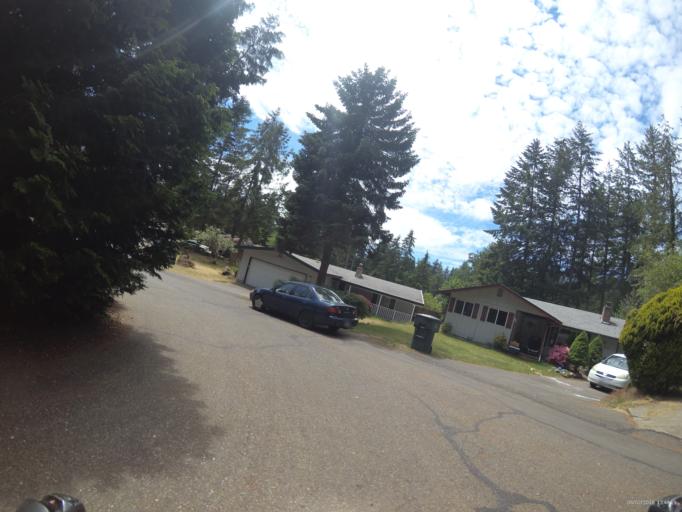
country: US
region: Washington
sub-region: Pierce County
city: University Place
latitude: 47.2095
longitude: -122.5602
